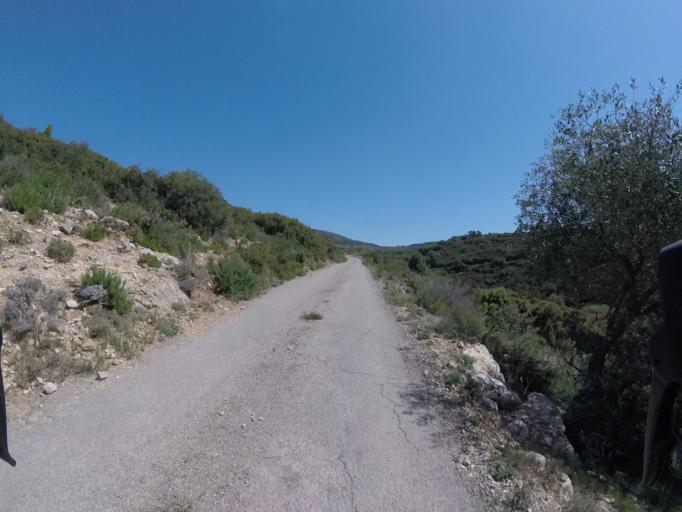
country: ES
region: Valencia
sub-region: Provincia de Castello
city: Sierra-Engarceran
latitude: 40.2526
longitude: -0.0257
